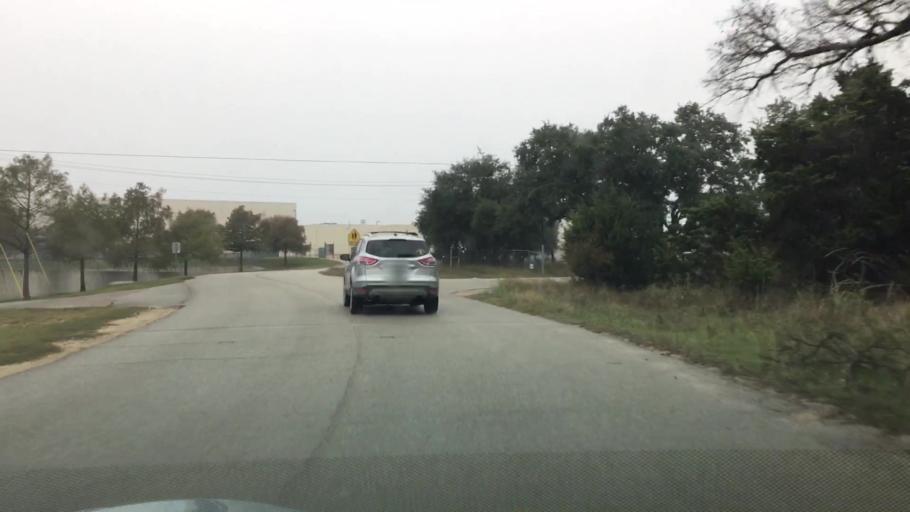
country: US
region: Texas
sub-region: Hays County
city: Dripping Springs
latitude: 30.1970
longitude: -98.0983
